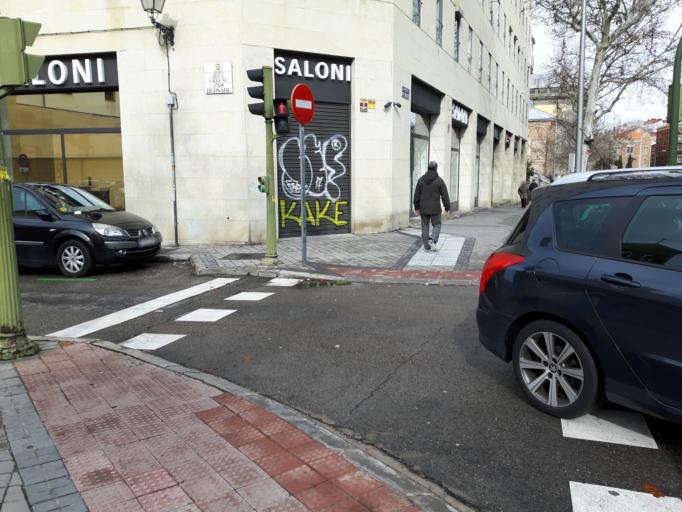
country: ES
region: Madrid
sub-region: Provincia de Madrid
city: Madrid
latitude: 40.4092
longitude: -3.7135
